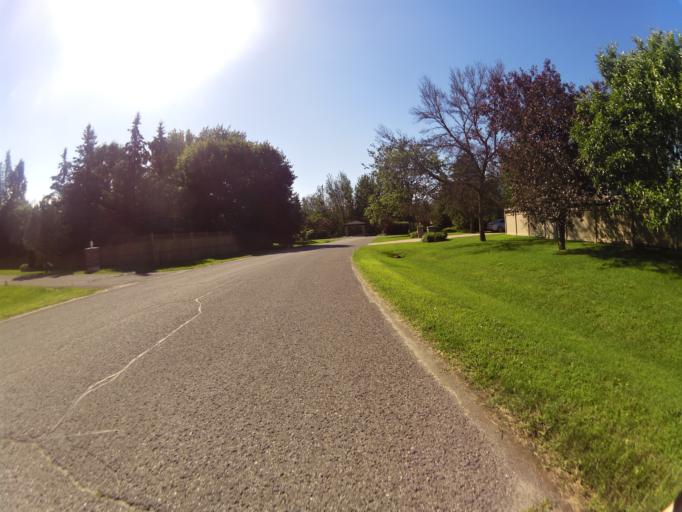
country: CA
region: Ontario
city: Bells Corners
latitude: 45.2789
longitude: -75.7841
